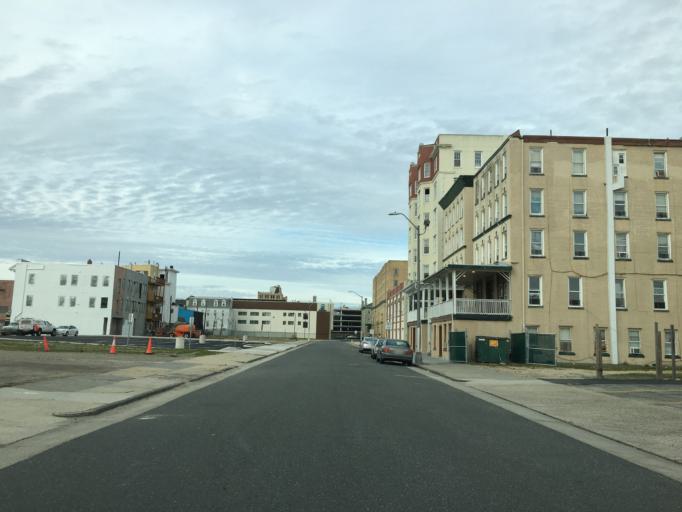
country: US
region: New Jersey
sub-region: Atlantic County
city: Atlantic City
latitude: 39.3585
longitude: -74.4265
